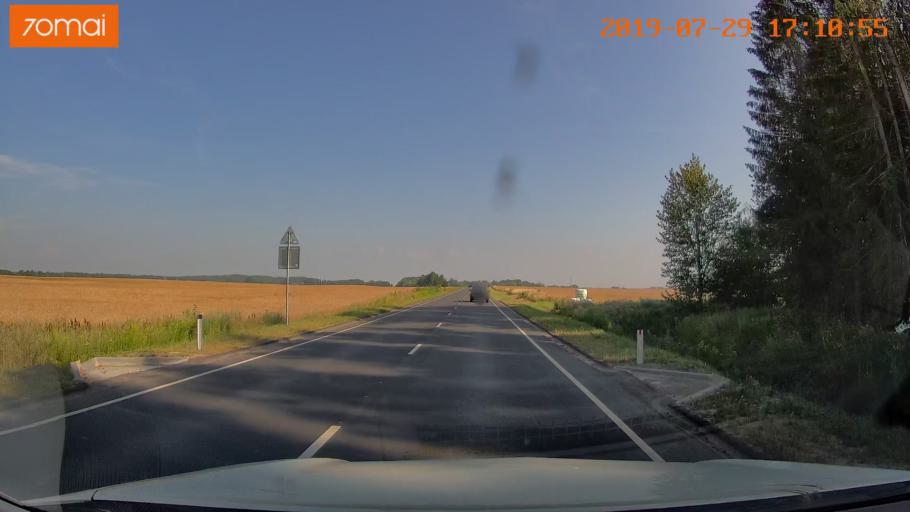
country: RU
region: Kaliningrad
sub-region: Gorod Kaliningrad
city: Kaliningrad
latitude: 54.7988
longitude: 20.3740
